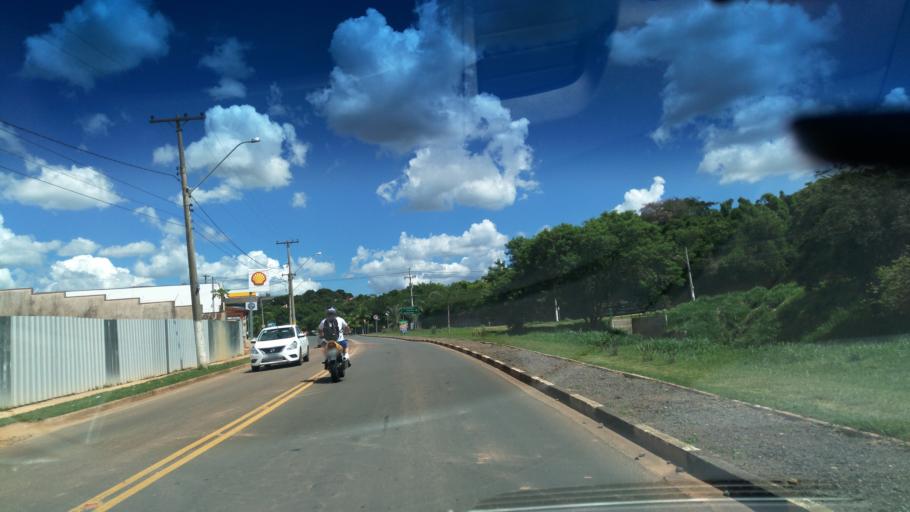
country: BR
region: Sao Paulo
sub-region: Valinhos
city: Valinhos
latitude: -22.9751
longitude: -47.0149
